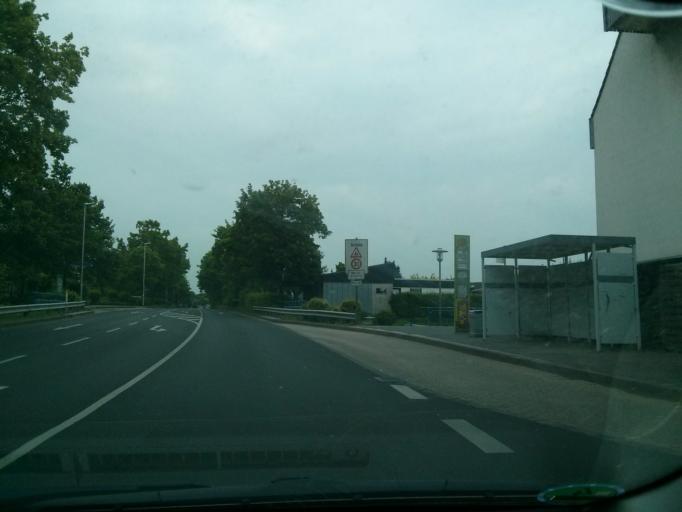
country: DE
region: North Rhine-Westphalia
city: Meckenheim
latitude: 50.6240
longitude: 7.0396
